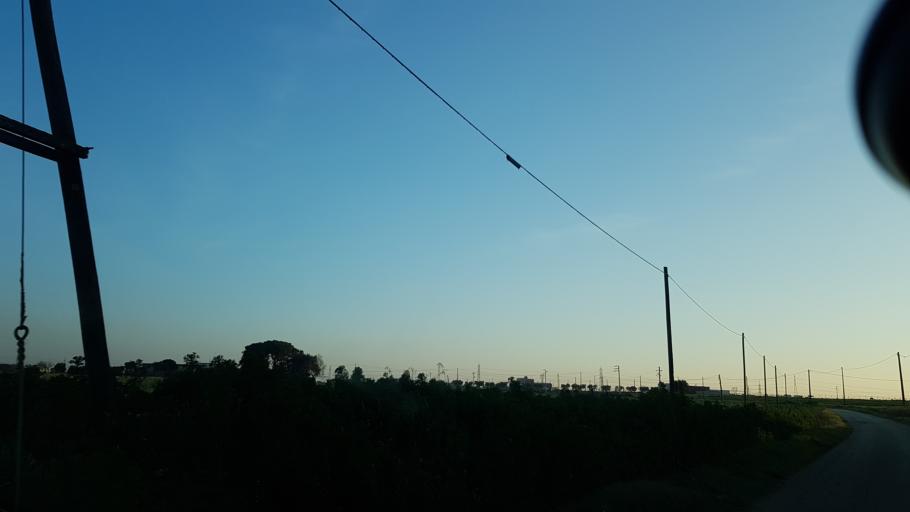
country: IT
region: Apulia
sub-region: Provincia di Brindisi
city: La Rosa
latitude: 40.6097
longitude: 17.9390
